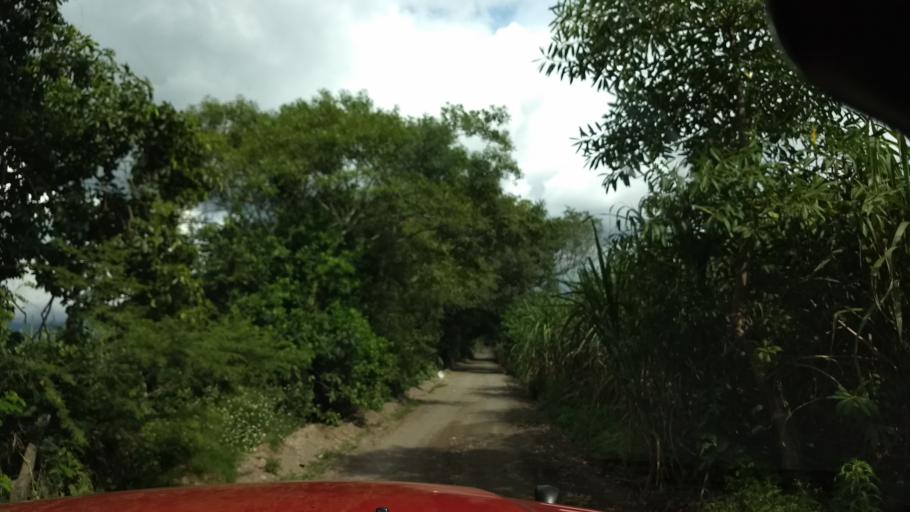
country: MX
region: Colima
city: Suchitlan
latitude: 19.4616
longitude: -103.7571
